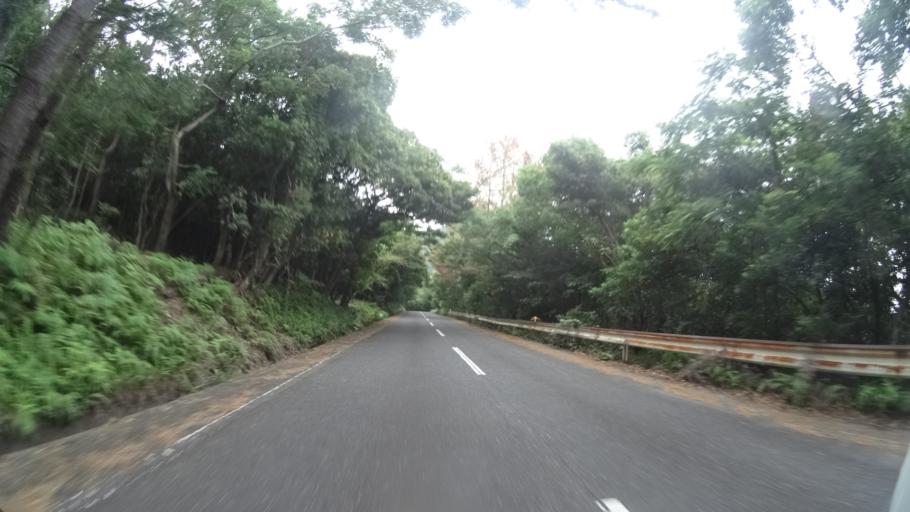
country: JP
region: Kagoshima
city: Nishinoomote
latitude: 30.3007
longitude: 130.4099
